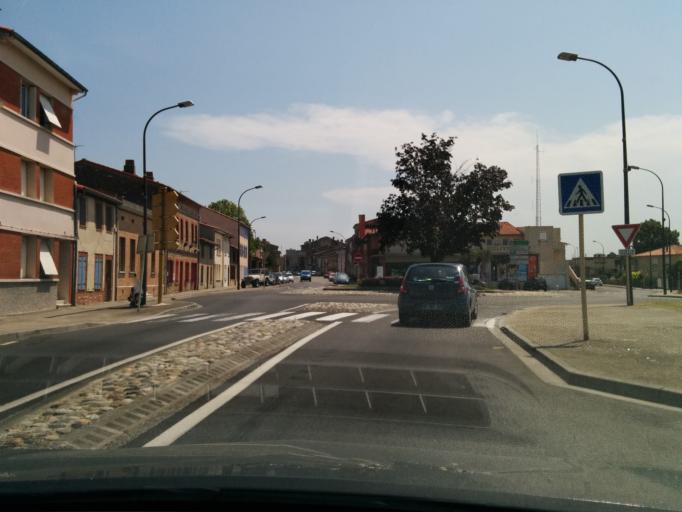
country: FR
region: Midi-Pyrenees
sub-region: Departement de la Haute-Garonne
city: Villefranche-de-Lauragais
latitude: 43.4022
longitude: 1.7129
